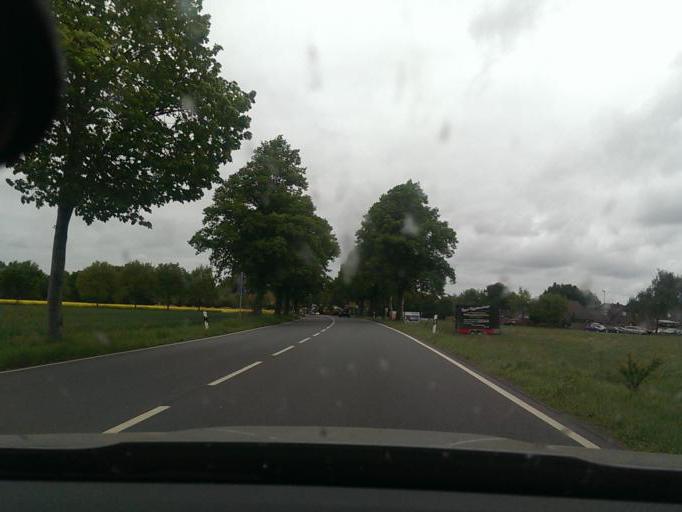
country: DE
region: Lower Saxony
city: Langenhagen
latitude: 52.4693
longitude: 9.7314
